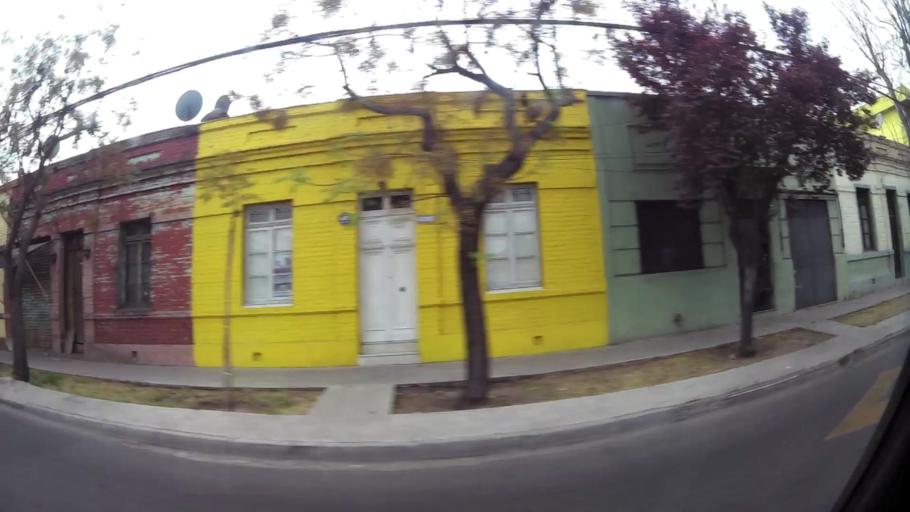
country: CL
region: Santiago Metropolitan
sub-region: Provincia de Santiago
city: Santiago
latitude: -33.4650
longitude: -70.6550
